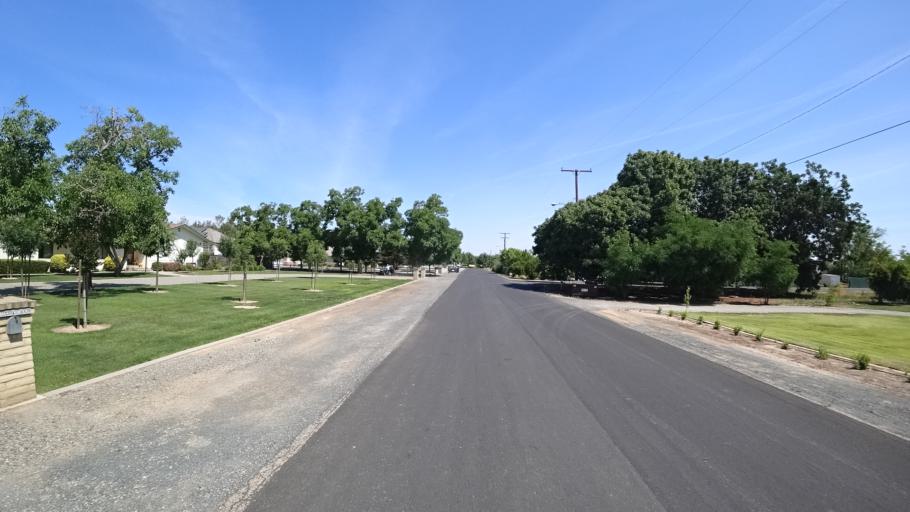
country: US
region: California
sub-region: Kings County
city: Armona
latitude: 36.3446
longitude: -119.7056
